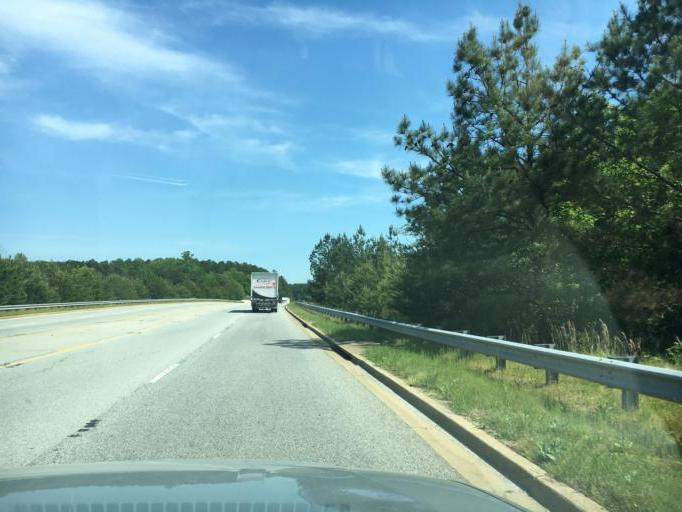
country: US
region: South Carolina
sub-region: Cherokee County
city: Blacksburg
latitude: 35.1294
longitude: -81.5063
